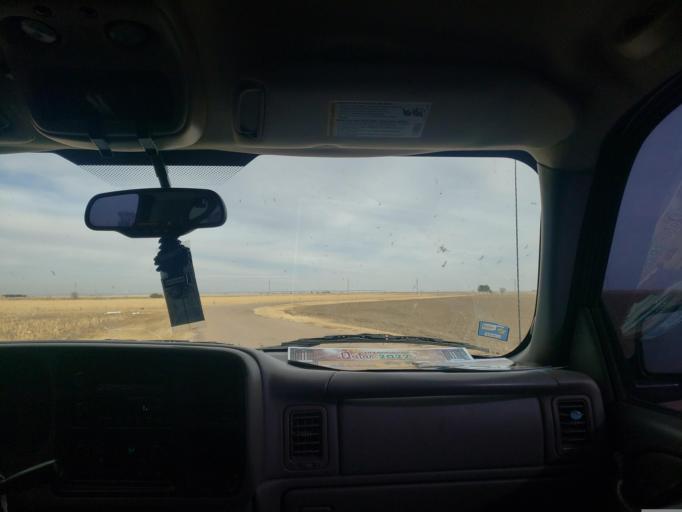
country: US
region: Kansas
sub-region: Finney County
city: Garden City
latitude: 37.9237
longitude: -100.7141
